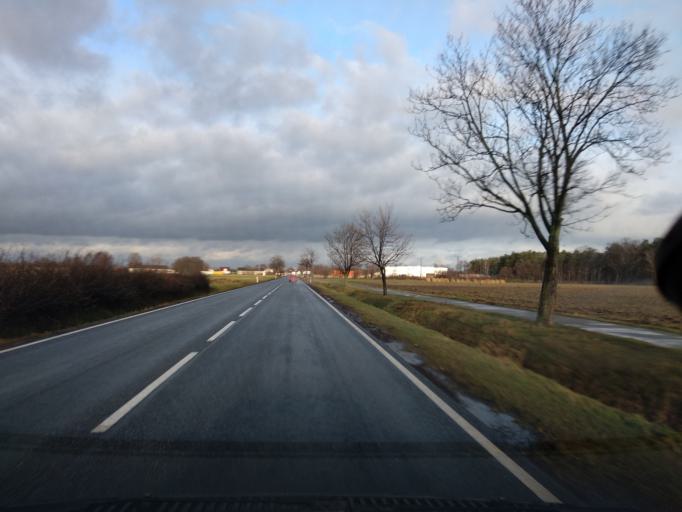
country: PL
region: Greater Poland Voivodeship
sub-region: Powiat koninski
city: Rychwal
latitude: 52.0898
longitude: 18.1644
